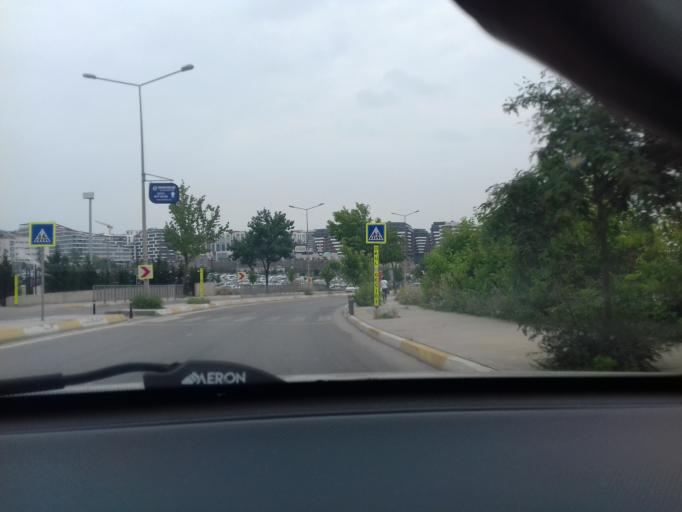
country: TR
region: Istanbul
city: Sultanbeyli
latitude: 40.9222
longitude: 29.3088
